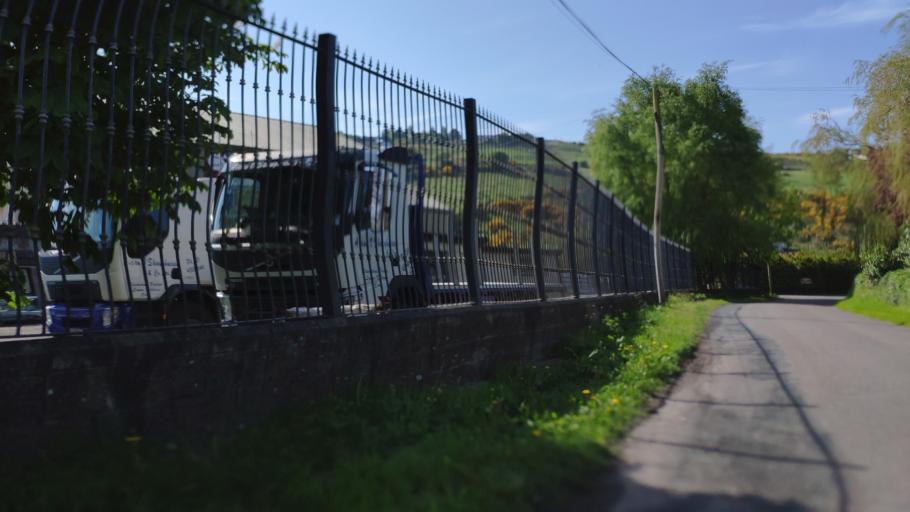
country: IE
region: Munster
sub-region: County Cork
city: Cork
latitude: 51.9193
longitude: -8.5042
